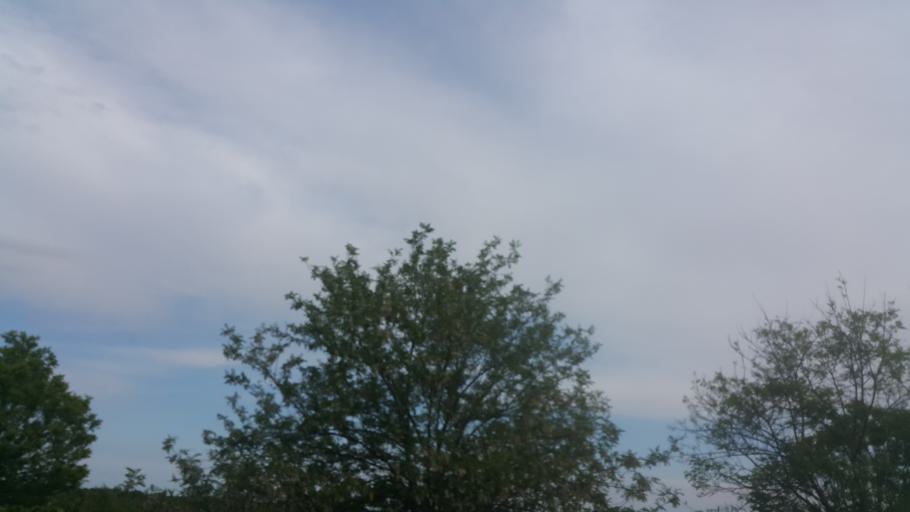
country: TR
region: Mersin
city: Yenice
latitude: 36.9598
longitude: 35.0123
